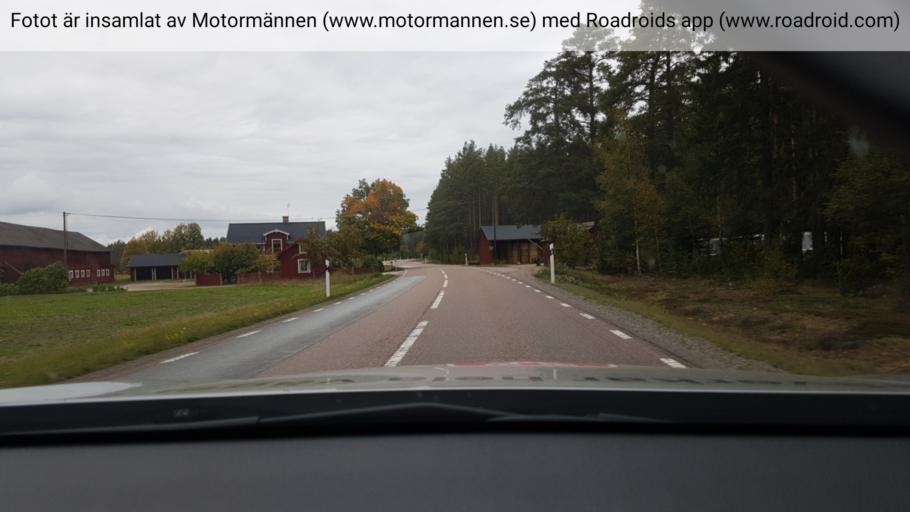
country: SE
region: Gaevleborg
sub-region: Gavle Kommun
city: Hedesunda
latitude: 60.4373
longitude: 16.9690
